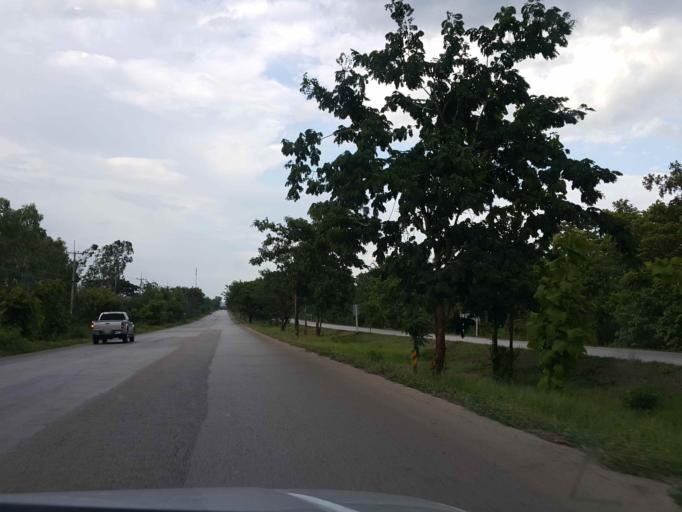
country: TH
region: Lampang
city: Soem Ngam
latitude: 18.0148
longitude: 99.3608
